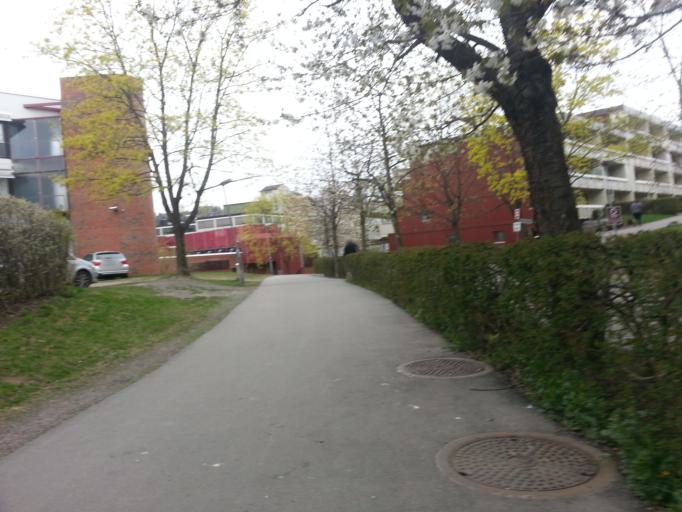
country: NO
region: Oslo
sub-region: Oslo
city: Sjolyststranda
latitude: 59.9255
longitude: 10.6802
